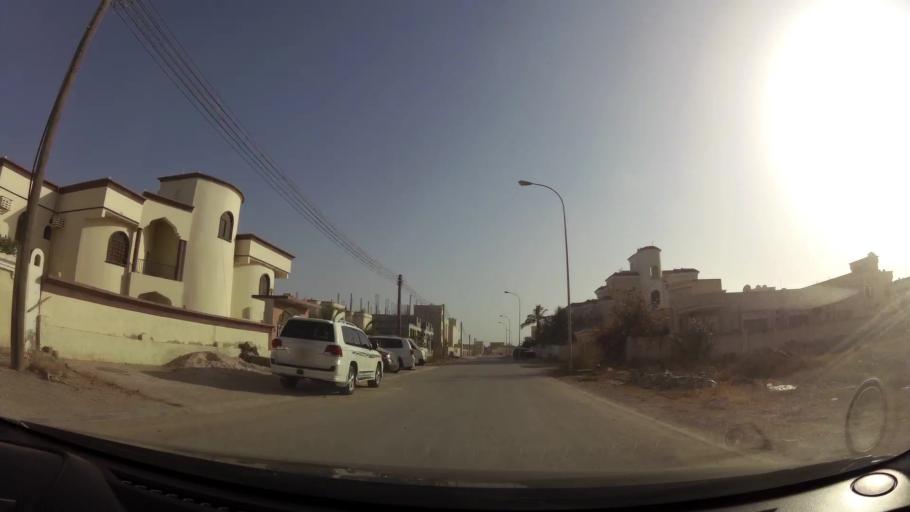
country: OM
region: Zufar
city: Salalah
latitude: 17.0183
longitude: 54.0223
